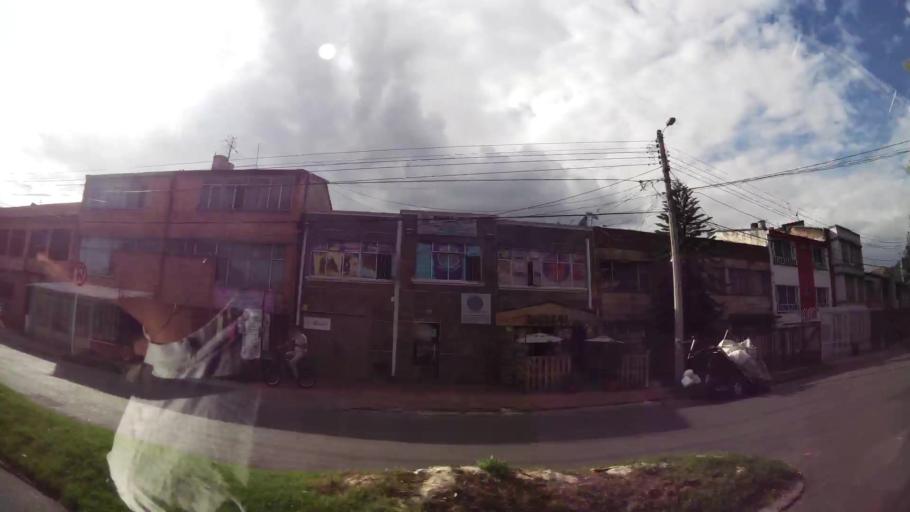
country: CO
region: Bogota D.C.
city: Bogota
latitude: 4.6444
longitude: -74.0738
